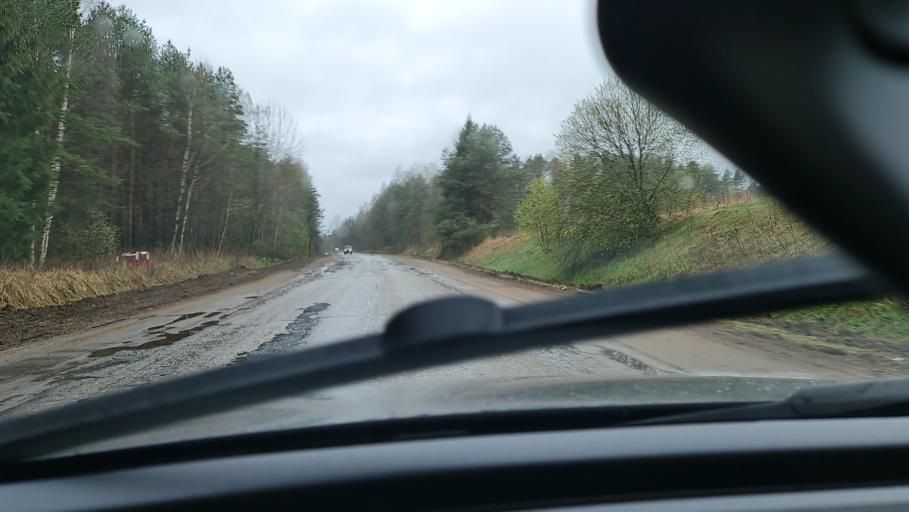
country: RU
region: Novgorod
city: Valday
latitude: 58.0409
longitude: 32.9188
